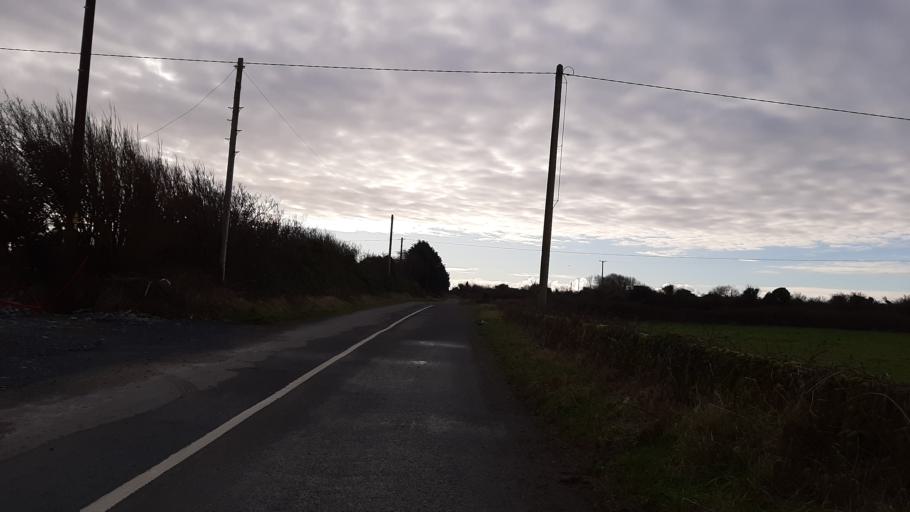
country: IE
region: Connaught
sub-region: County Galway
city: Gaillimh
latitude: 53.3124
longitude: -9.0667
